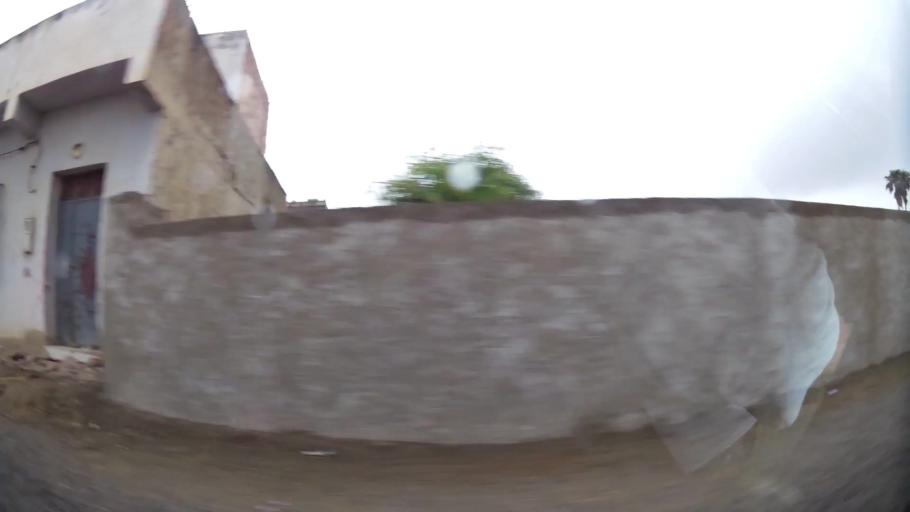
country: MA
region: Oriental
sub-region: Nador
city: Nador
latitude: 35.1542
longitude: -2.9580
